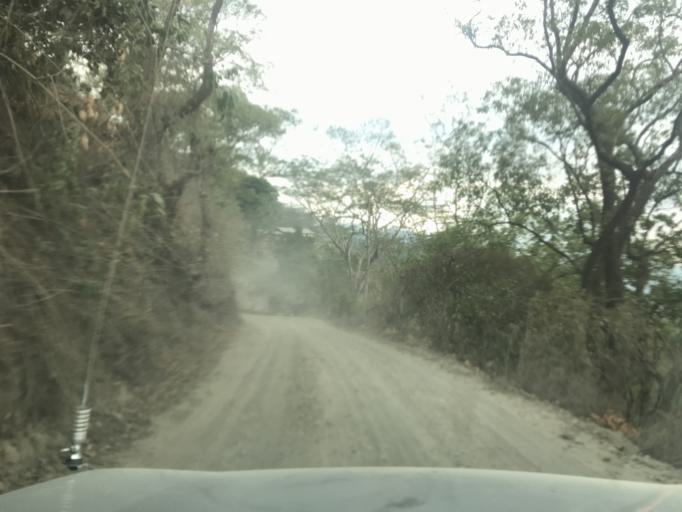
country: TL
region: Ermera
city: Gleno
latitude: -8.7633
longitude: 125.4367
